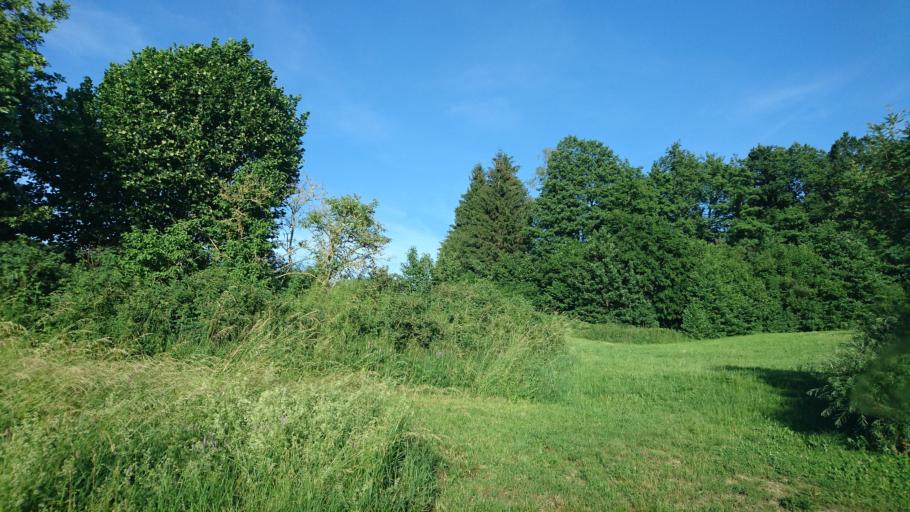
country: DE
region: Bavaria
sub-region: Swabia
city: Altenmunster
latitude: 48.4772
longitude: 10.6052
